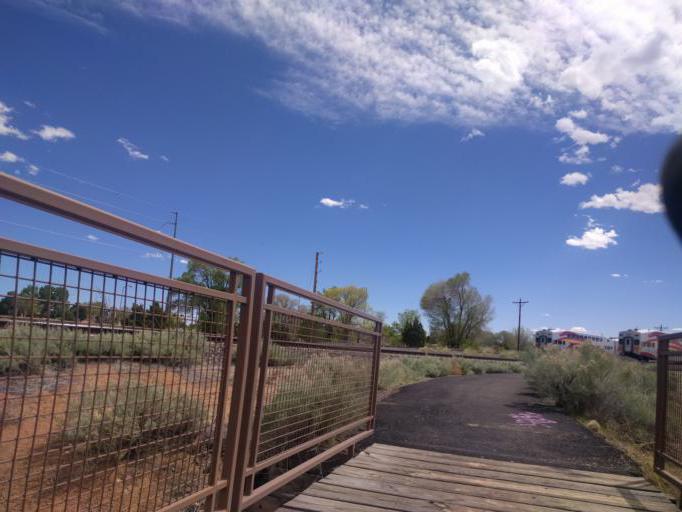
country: US
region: New Mexico
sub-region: Santa Fe County
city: Santa Fe
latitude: 35.6438
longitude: -105.9575
